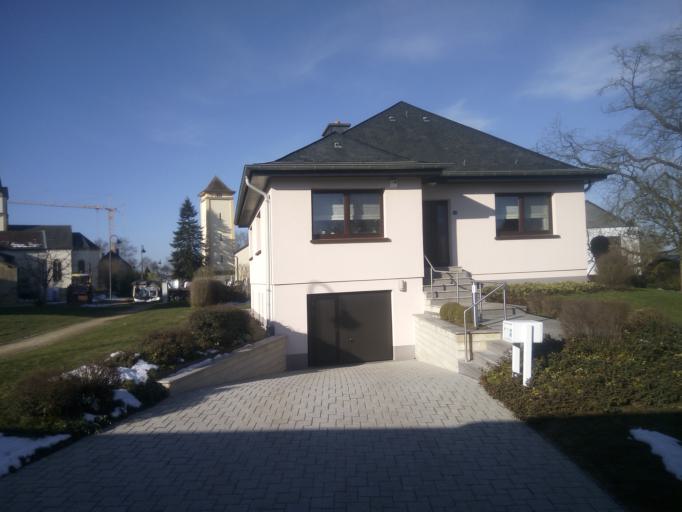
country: LU
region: Grevenmacher
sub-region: Canton d'Echternach
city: Consdorf
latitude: 49.7506
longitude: 6.3283
